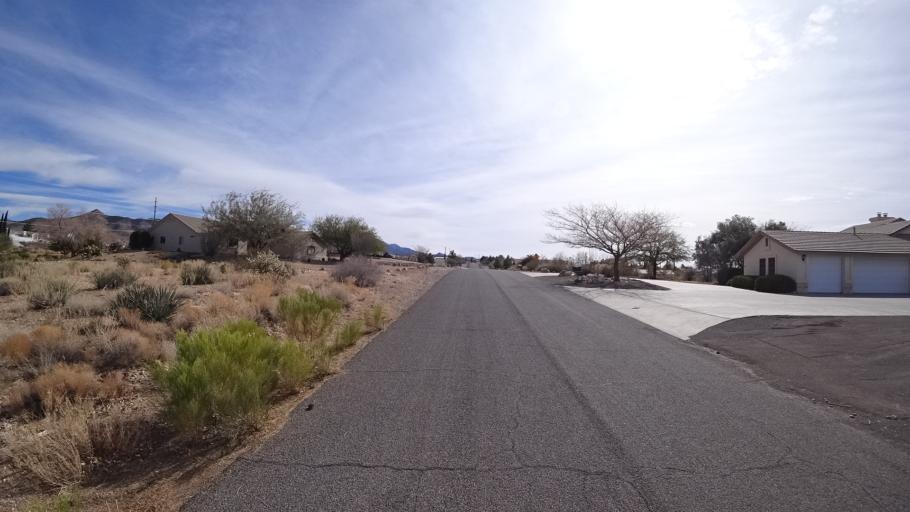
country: US
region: Arizona
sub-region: Mohave County
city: Kingman
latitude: 35.1893
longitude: -113.9865
